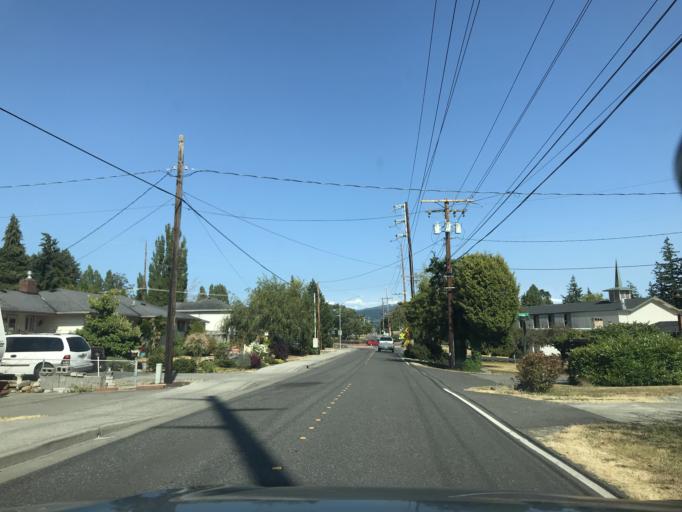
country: US
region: Washington
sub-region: Whatcom County
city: Bellingham
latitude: 48.7824
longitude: -122.5046
